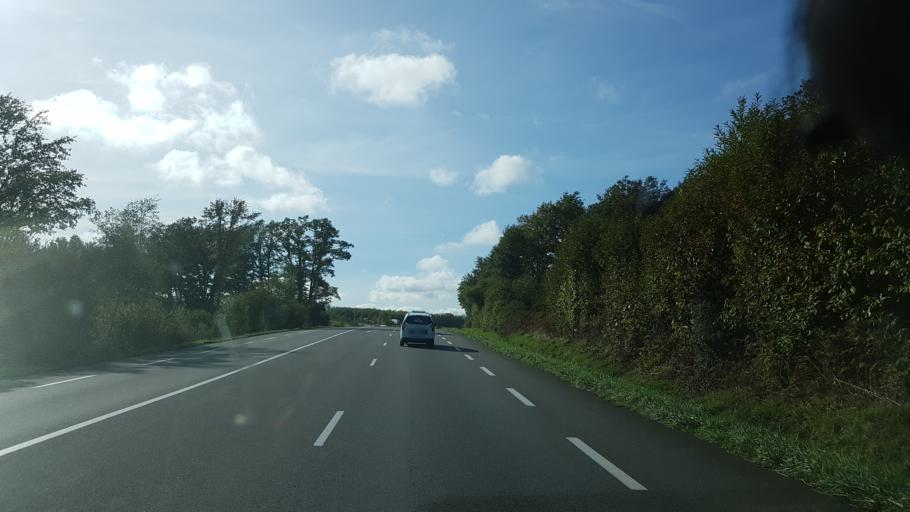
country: FR
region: Poitou-Charentes
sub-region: Departement de la Charente
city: Saint-Claud
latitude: 45.9159
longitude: 0.5022
